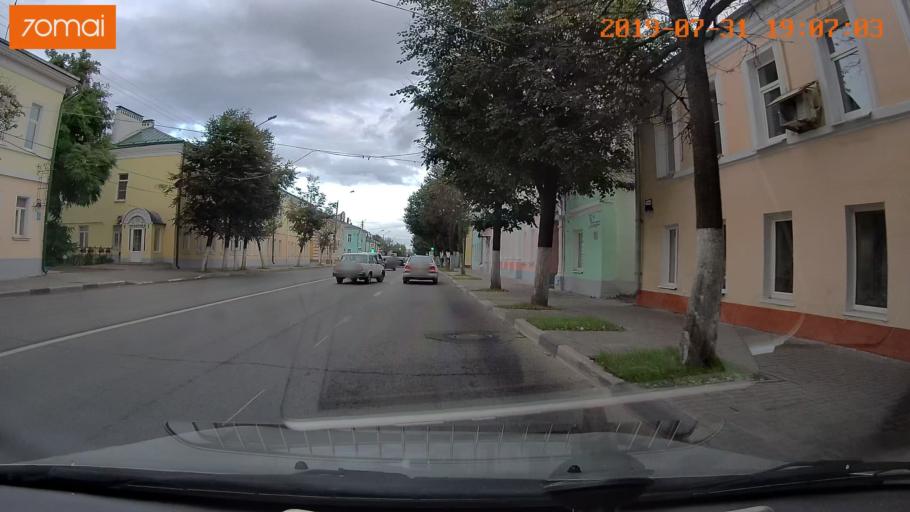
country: RU
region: Moskovskaya
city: Kolomna
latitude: 55.0994
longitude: 38.7585
